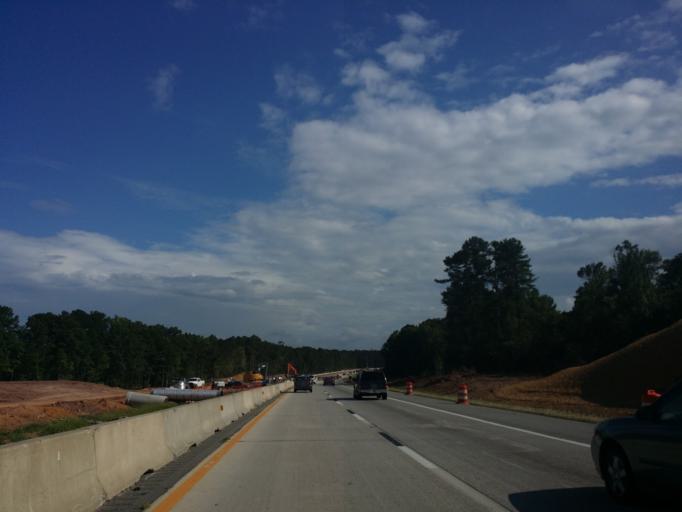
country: US
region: North Carolina
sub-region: Durham County
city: Durham
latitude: 35.9657
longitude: -78.8664
